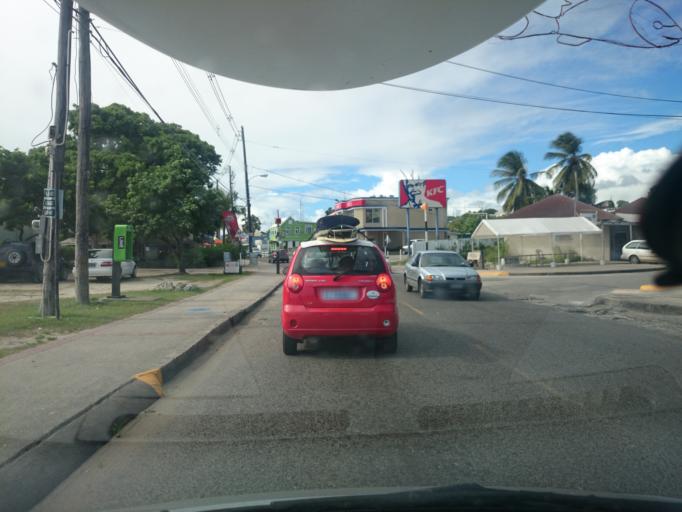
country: BB
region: Christ Church
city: Oistins
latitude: 13.0631
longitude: -59.5418
